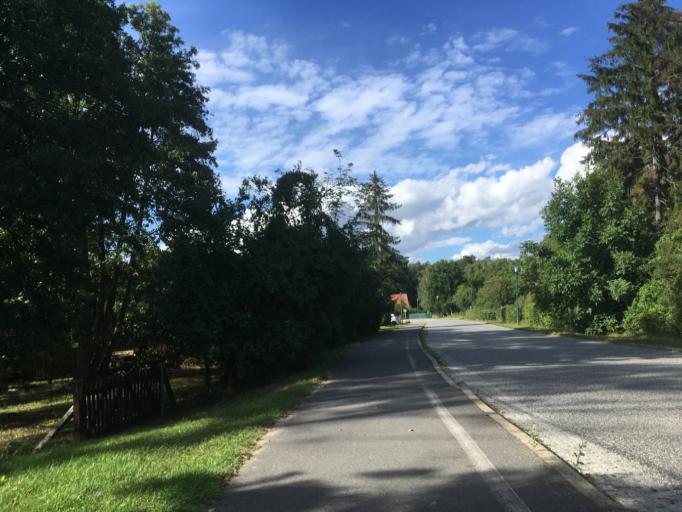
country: DE
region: Brandenburg
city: Liepe
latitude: 52.9177
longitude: 13.9523
